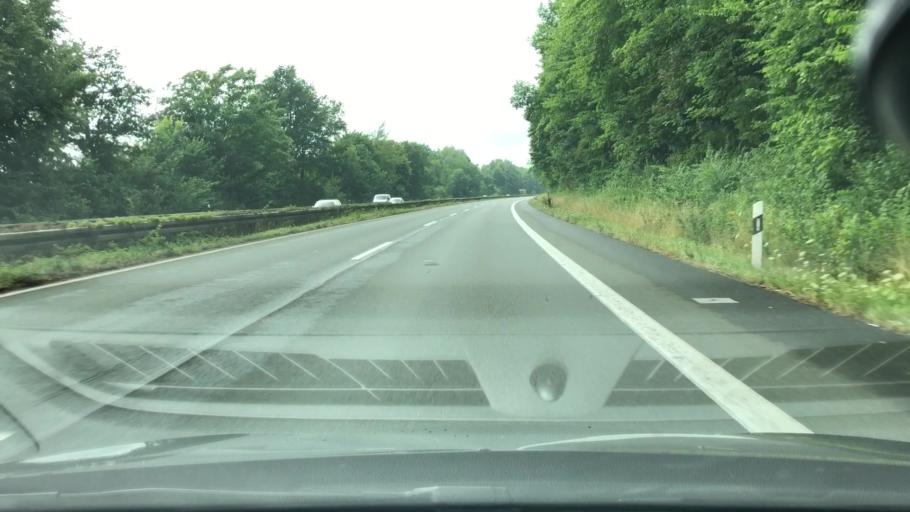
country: DE
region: Lower Saxony
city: Buckeburg
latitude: 52.2595
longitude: 9.0058
